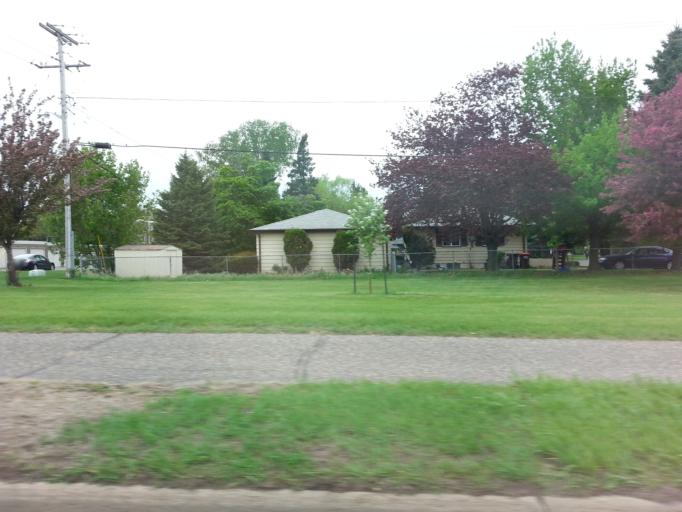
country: US
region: Minnesota
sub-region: Washington County
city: Oakdale
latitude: 44.9647
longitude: -92.9646
